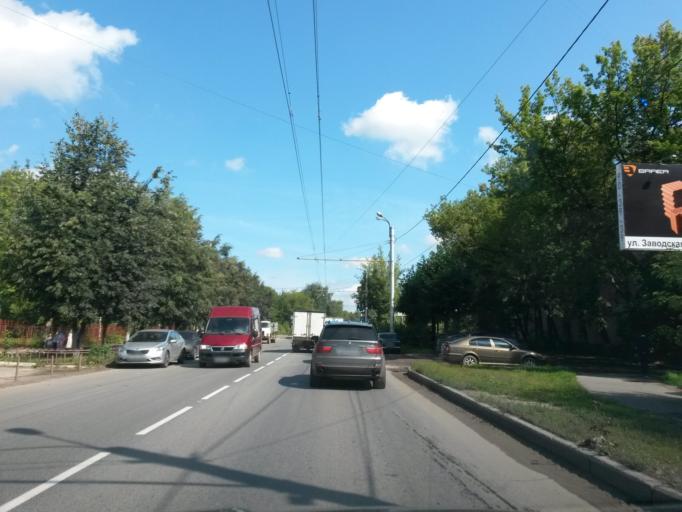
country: RU
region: Ivanovo
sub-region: Gorod Ivanovo
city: Ivanovo
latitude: 57.0017
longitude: 40.9437
